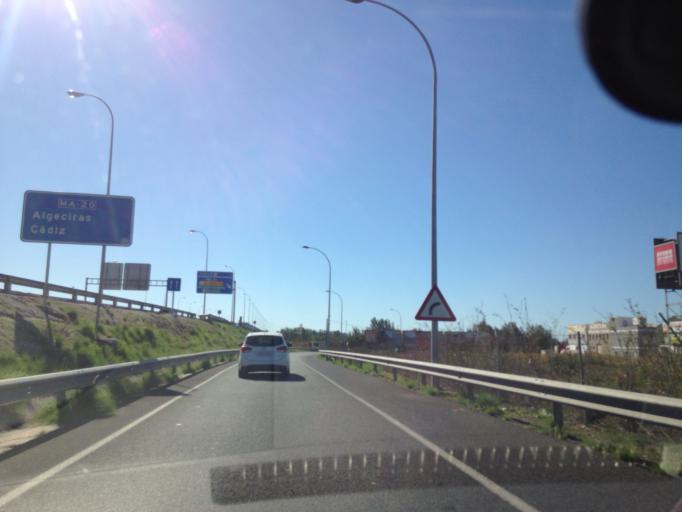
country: ES
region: Andalusia
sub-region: Provincia de Malaga
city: Malaga
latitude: 36.6820
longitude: -4.4632
